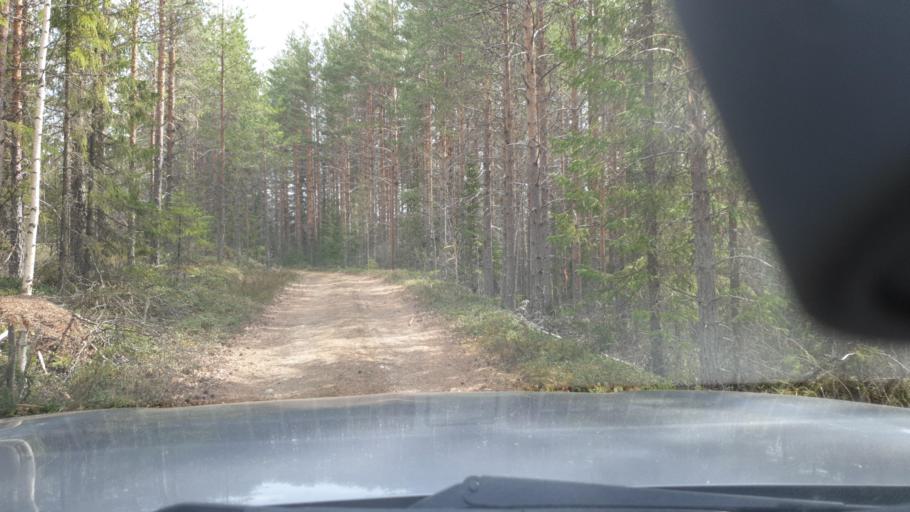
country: SE
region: Vaesternorrland
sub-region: Ange Kommun
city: Ange
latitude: 62.1893
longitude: 15.6040
